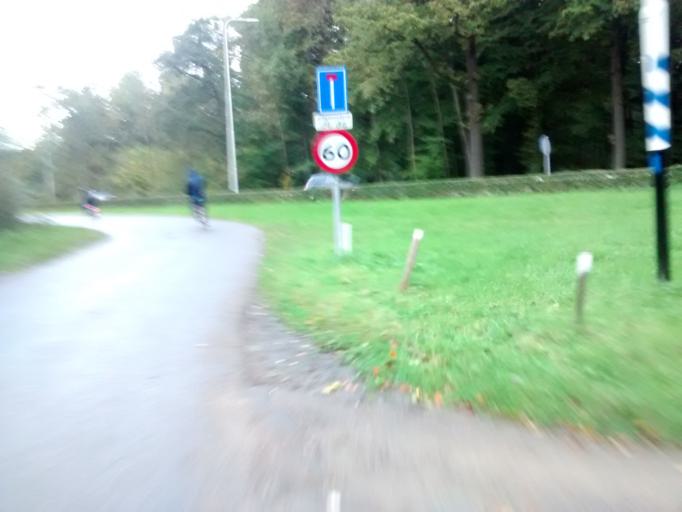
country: NL
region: Utrecht
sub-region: Gemeente Utrecht
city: Lunetten
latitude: 52.0692
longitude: 5.1510
